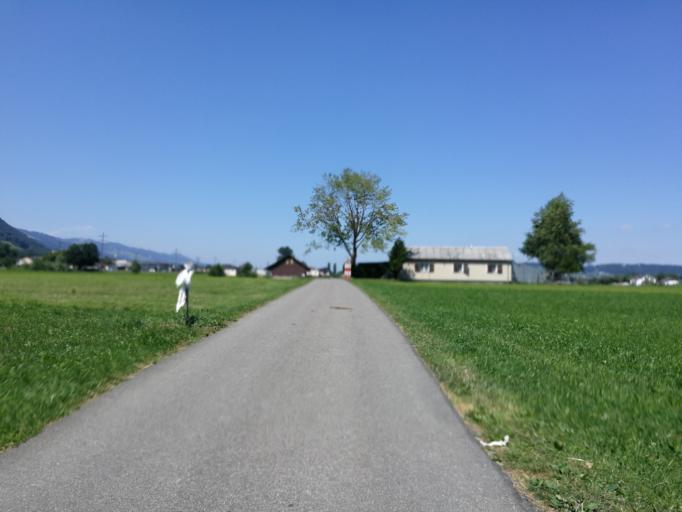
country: CH
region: Schwyz
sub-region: Bezirk March
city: Reichenburg
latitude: 47.1729
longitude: 8.9896
